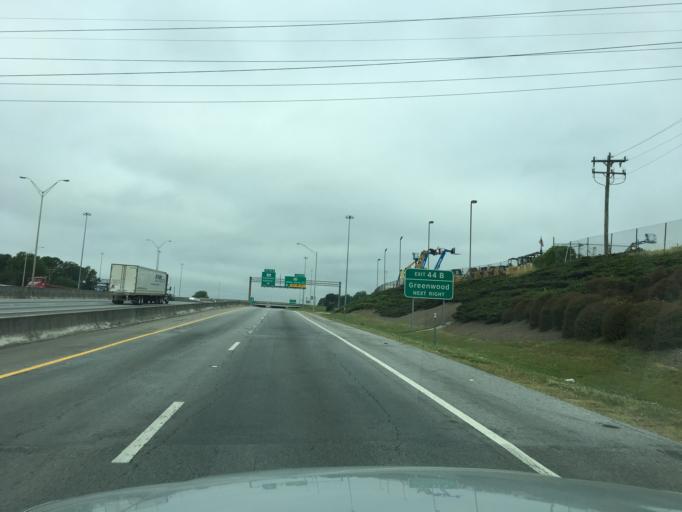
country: US
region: South Carolina
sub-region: Greenville County
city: Gantt
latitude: 34.7931
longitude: -82.4120
